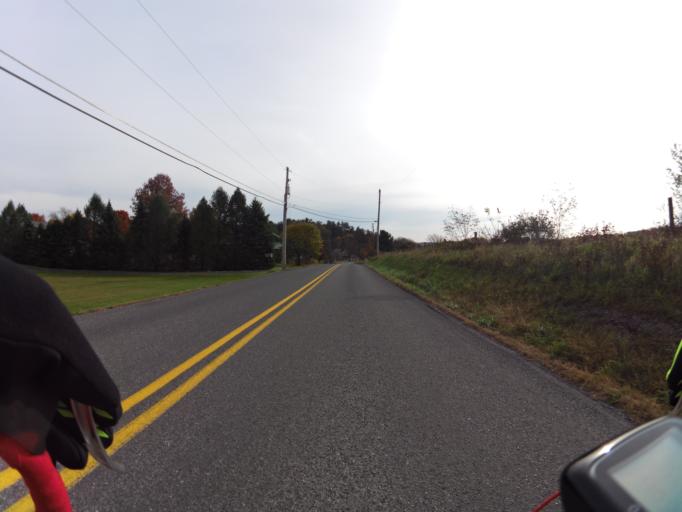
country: US
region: Pennsylvania
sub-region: Union County
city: New Columbia
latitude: 41.0454
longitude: -76.8847
